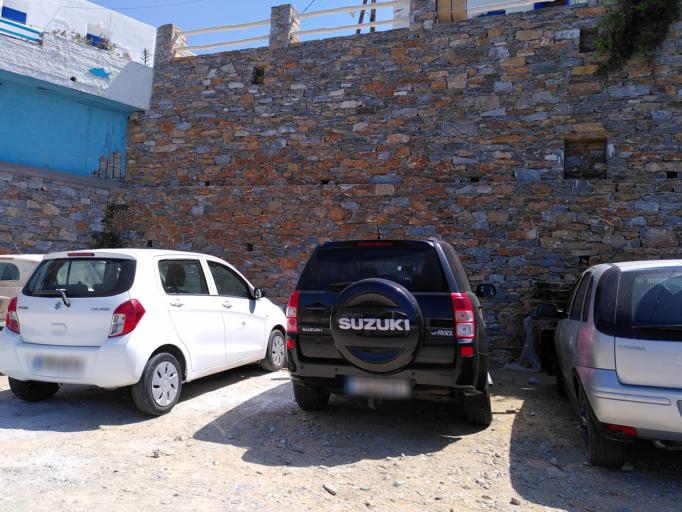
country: GR
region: South Aegean
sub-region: Nomos Kykladon
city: Amorgos
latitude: 36.9006
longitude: 25.9760
